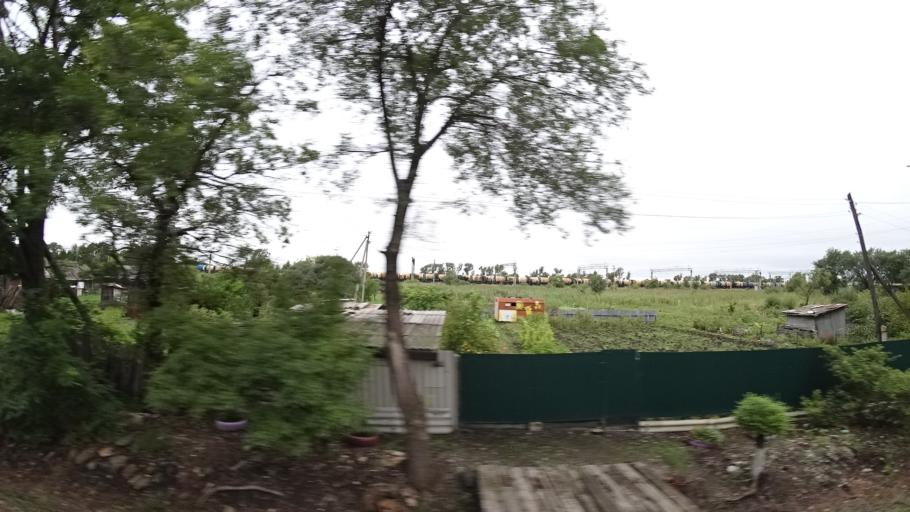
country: RU
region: Primorskiy
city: Chernigovka
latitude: 44.3371
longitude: 132.5324
